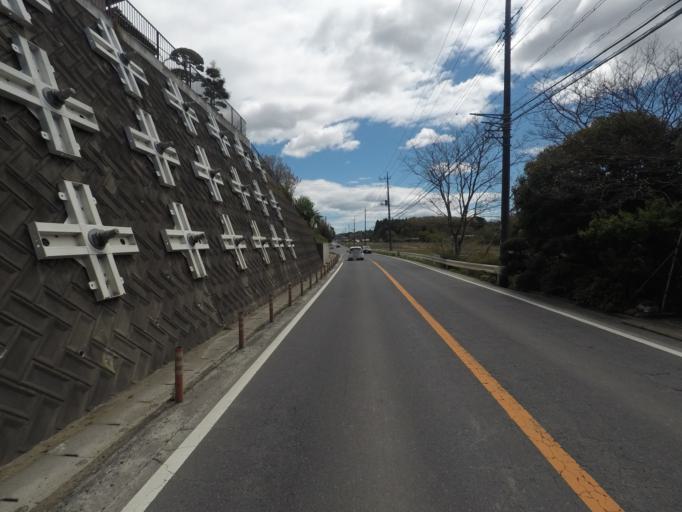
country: JP
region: Ibaraki
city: Okunoya
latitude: 36.1116
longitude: 140.4635
